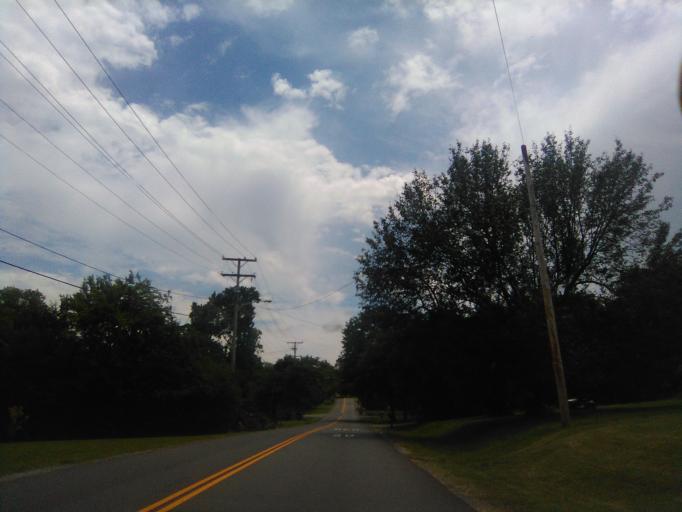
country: US
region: Tennessee
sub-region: Davidson County
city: Belle Meade
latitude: 36.1338
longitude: -86.8876
